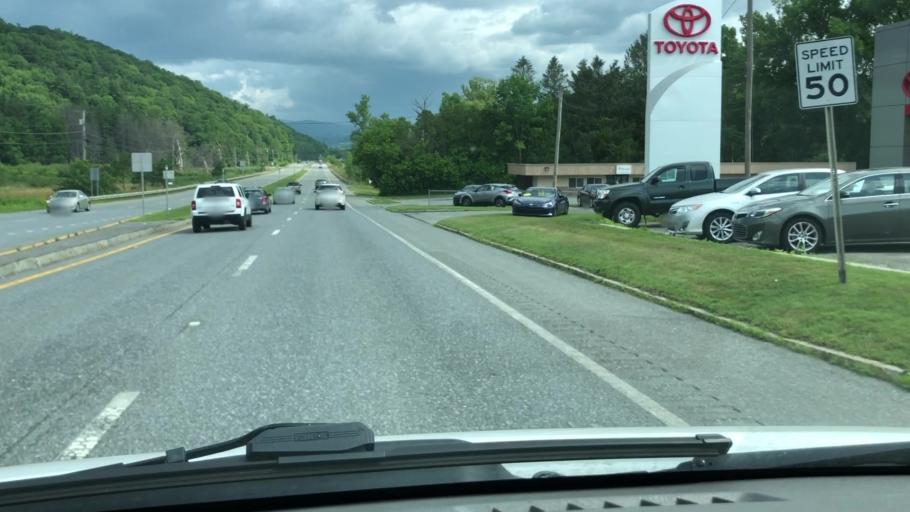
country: US
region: Massachusetts
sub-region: Berkshire County
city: North Adams
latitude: 42.6665
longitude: -73.1077
